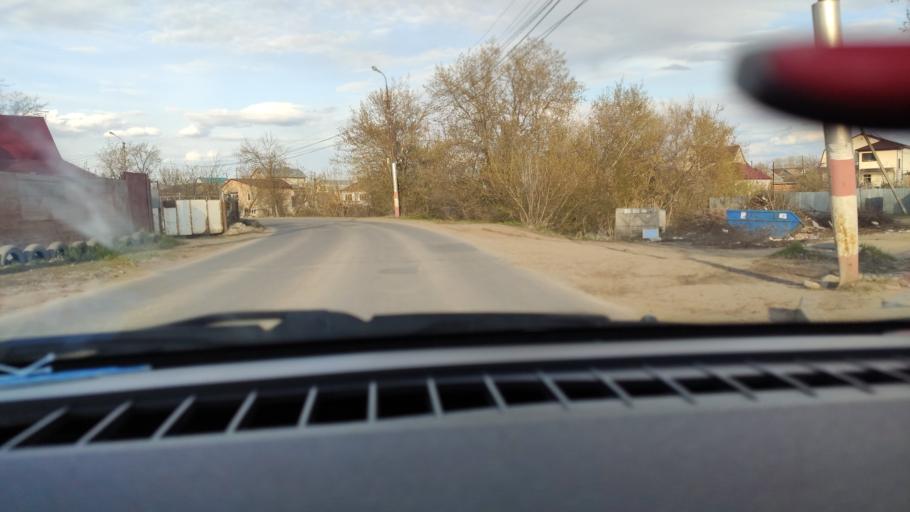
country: RU
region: Saratov
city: Engel's
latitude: 51.5001
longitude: 46.0642
